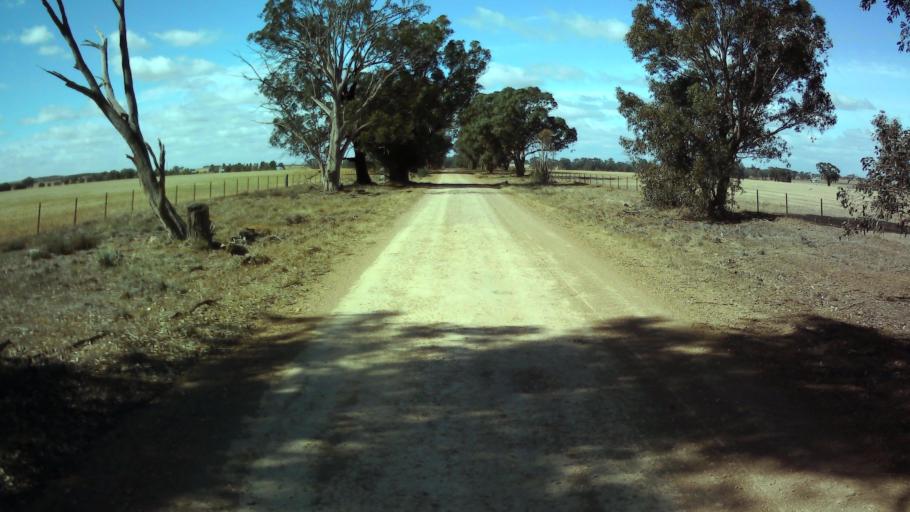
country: AU
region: New South Wales
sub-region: Weddin
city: Grenfell
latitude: -34.0534
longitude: 148.3134
